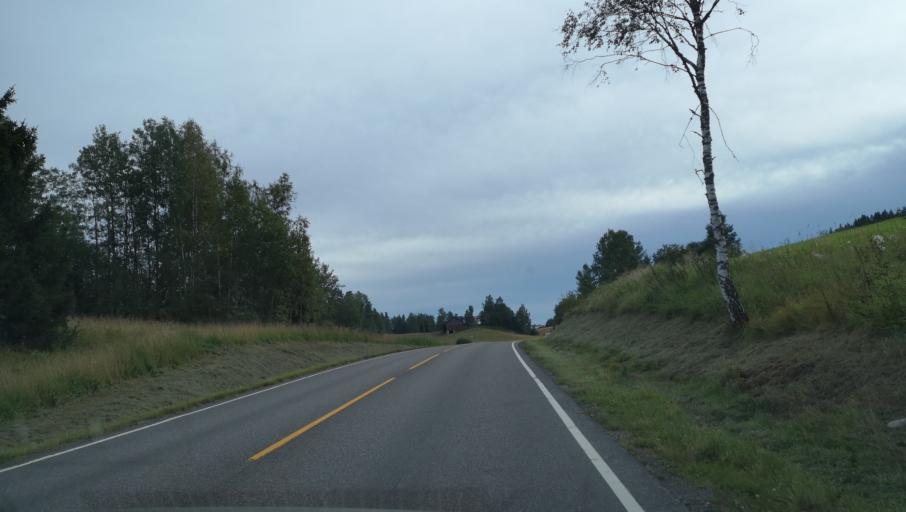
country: NO
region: Ostfold
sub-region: Hobol
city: Tomter
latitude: 59.7073
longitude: 11.0497
